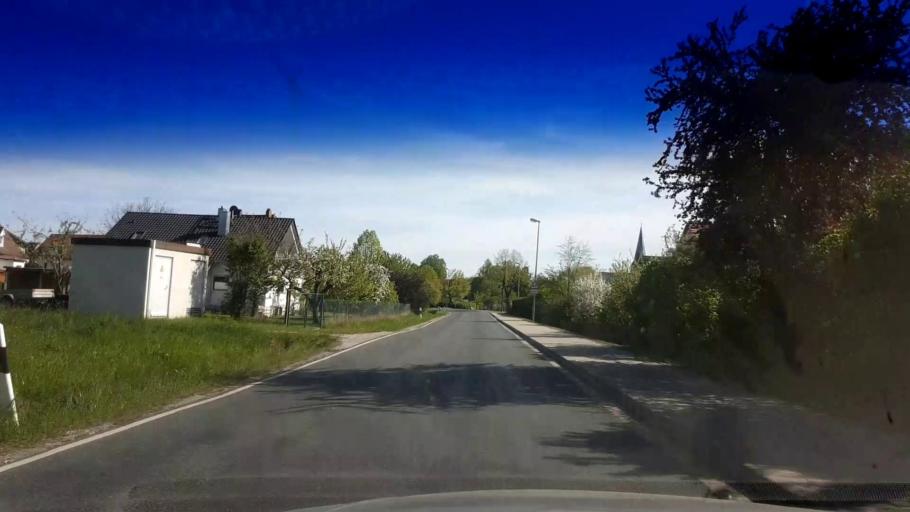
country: DE
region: Bavaria
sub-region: Upper Franconia
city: Buttenheim
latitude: 49.8060
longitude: 11.0310
